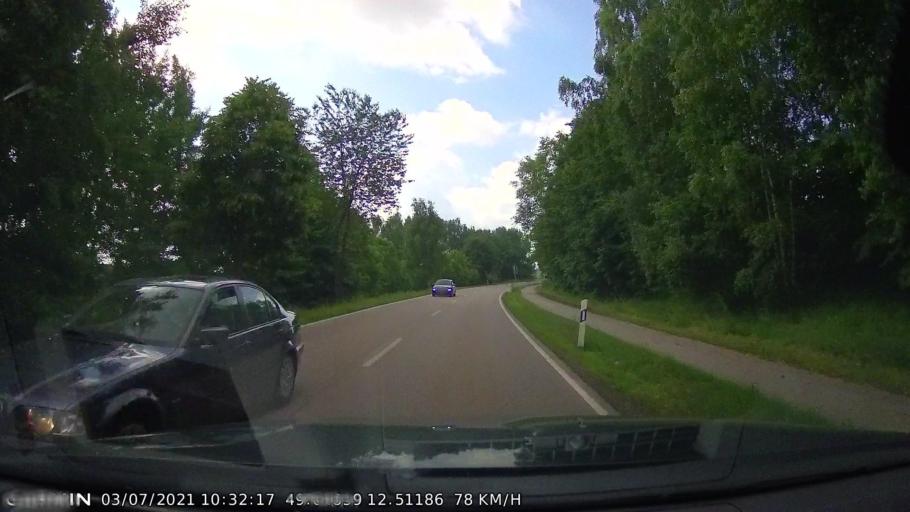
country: DE
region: Bavaria
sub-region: Upper Palatinate
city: Waidhaus
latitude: 49.6487
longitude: 12.5120
